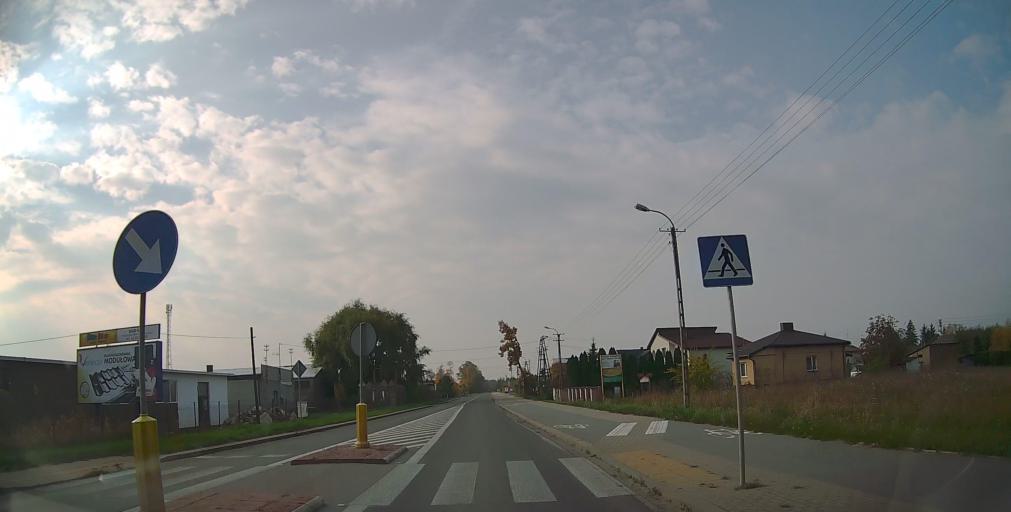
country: PL
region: Masovian Voivodeship
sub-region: Powiat grojecki
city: Mogielnica
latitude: 51.7067
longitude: 20.7382
